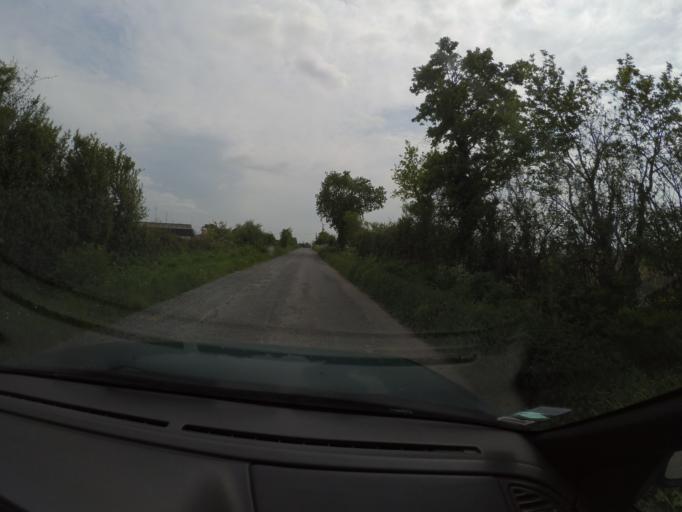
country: FR
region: Pays de la Loire
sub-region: Departement de la Loire-Atlantique
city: Saint-Lumine-de-Clisson
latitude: 47.0932
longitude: -1.3201
